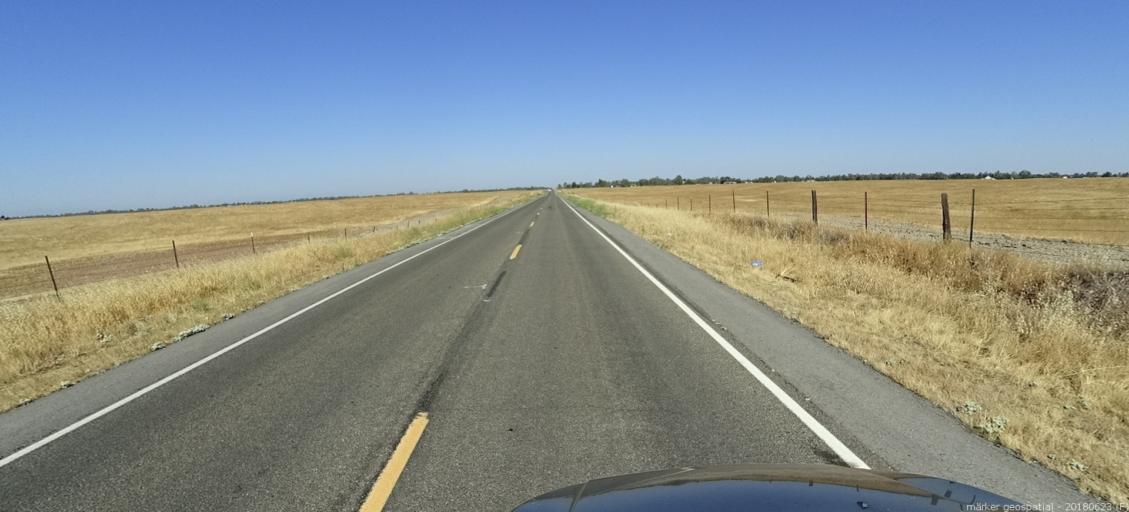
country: US
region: California
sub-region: Madera County
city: Bonadelle Ranchos-Madera Ranchos
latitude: 36.9666
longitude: -119.8631
